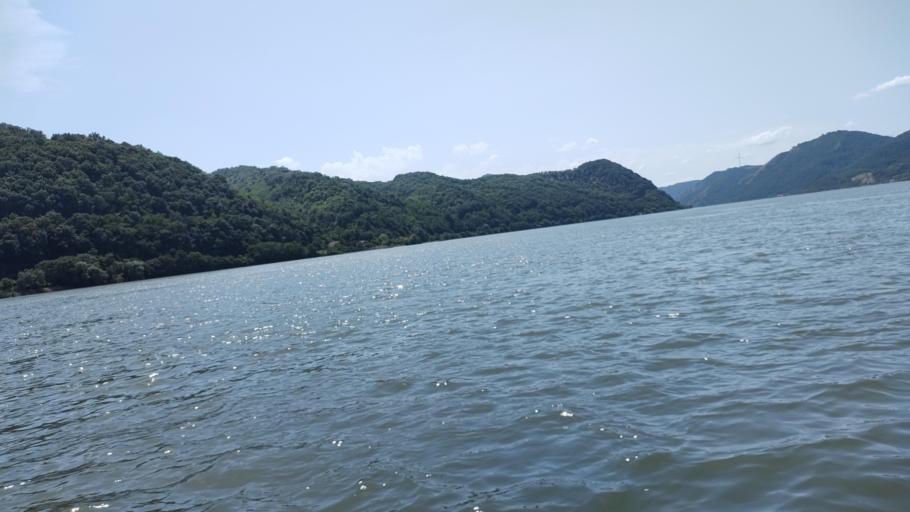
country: RS
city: Radenka
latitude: 44.6585
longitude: 21.7959
